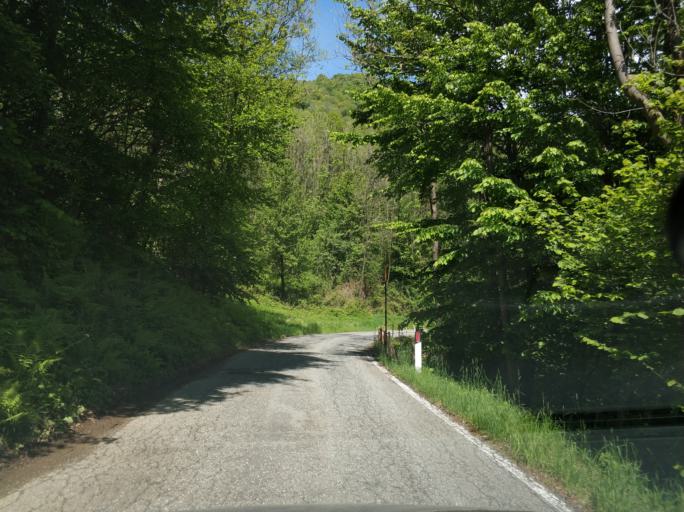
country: IT
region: Piedmont
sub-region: Provincia di Torino
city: Coassolo
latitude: 45.3125
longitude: 7.4706
